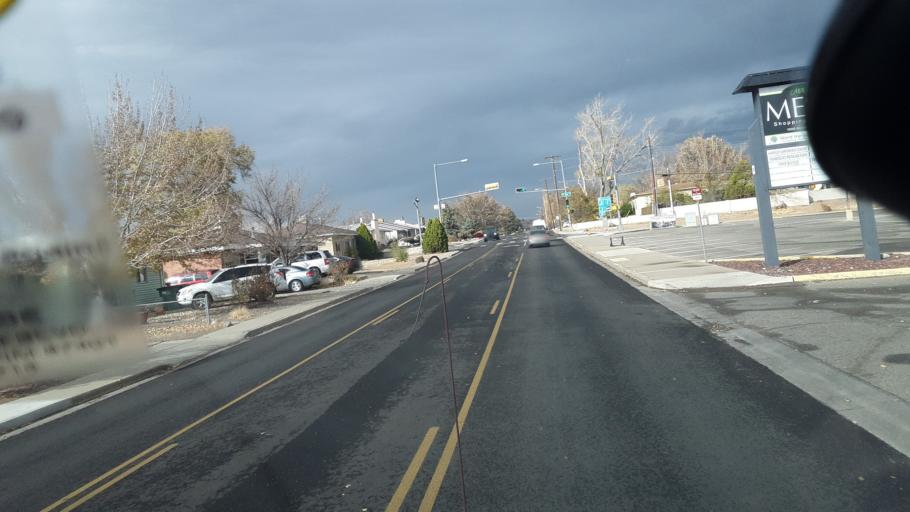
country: US
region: New Mexico
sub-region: San Juan County
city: Farmington
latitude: 36.7403
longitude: -108.1978
